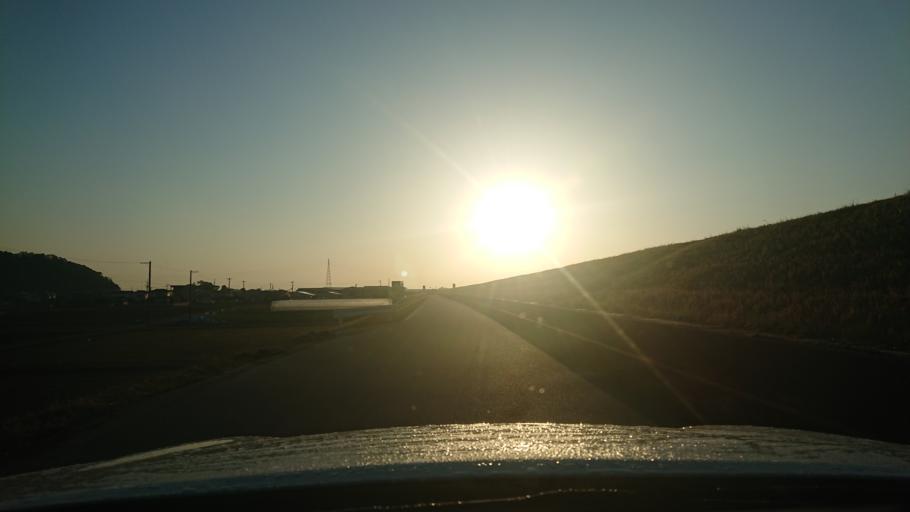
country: JP
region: Tokushima
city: Komatsushimacho
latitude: 33.9419
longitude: 134.5932
